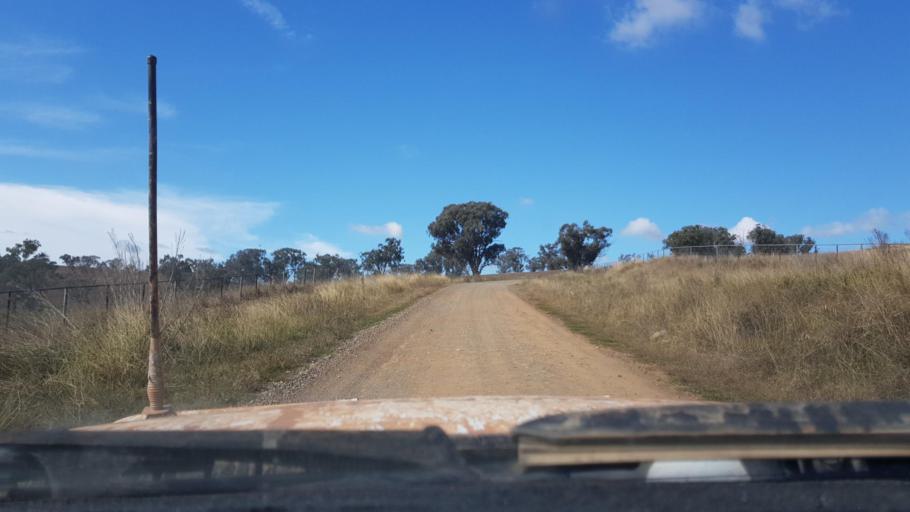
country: AU
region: New South Wales
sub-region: Boorowa
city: Boorowa
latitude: -34.1729
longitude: 148.8252
